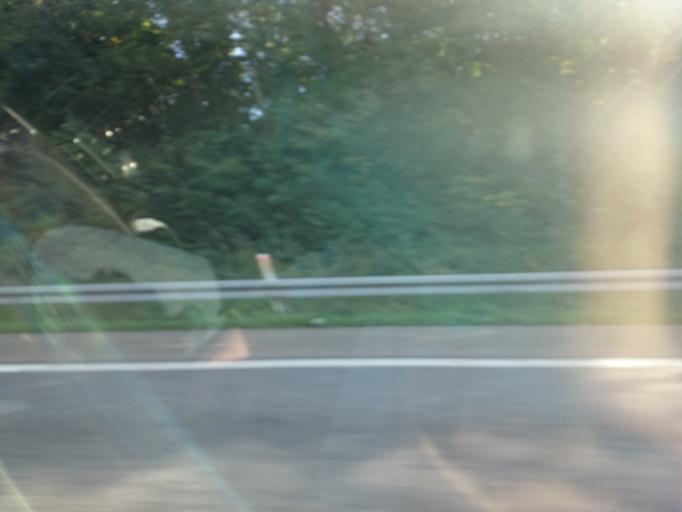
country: DK
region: Central Jutland
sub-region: Skanderborg Kommune
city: Skanderborg
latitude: 56.0401
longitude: 9.8929
